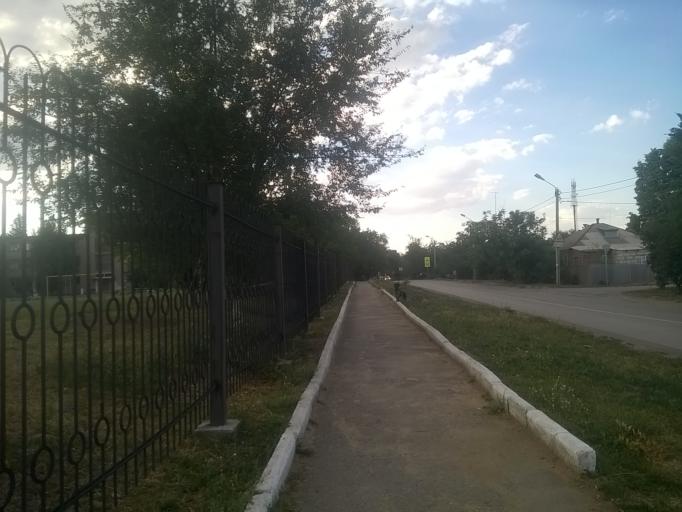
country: RU
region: Rostov
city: Donetsk
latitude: 48.3329
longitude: 39.9523
